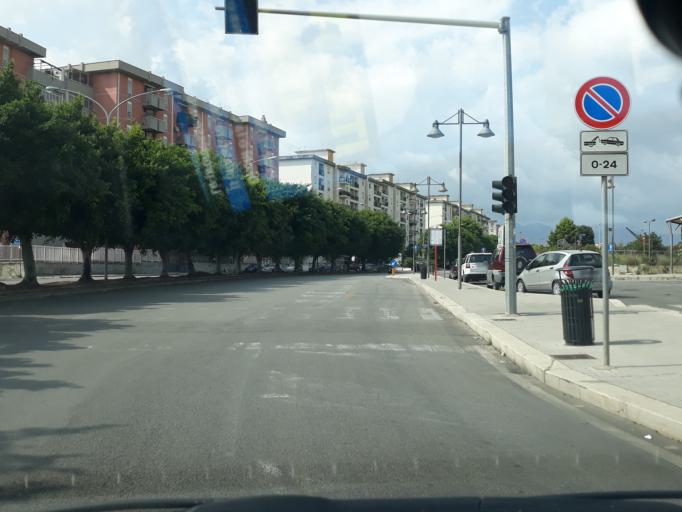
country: IT
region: Sicily
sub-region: Palermo
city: Palermo
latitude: 38.0979
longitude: 13.3459
